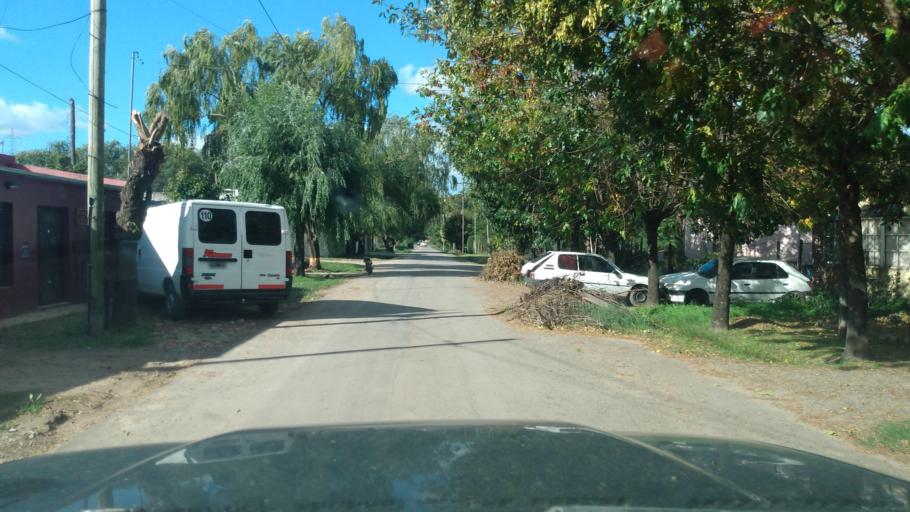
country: AR
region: Buenos Aires
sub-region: Partido de Lujan
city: Lujan
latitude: -34.5810
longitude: -59.0899
